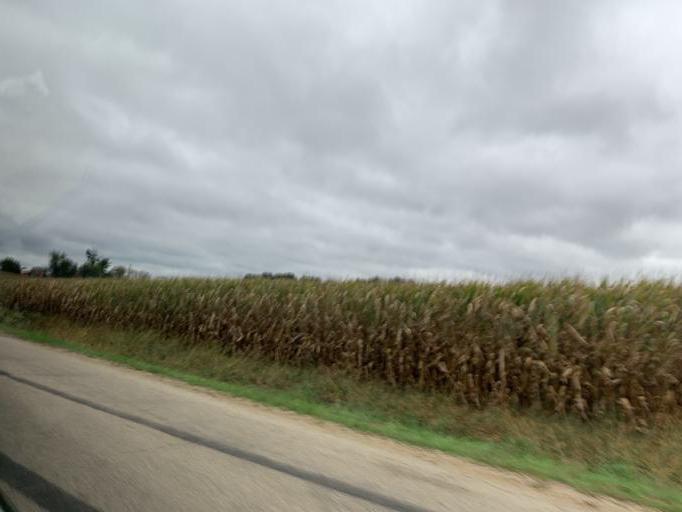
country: US
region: Wisconsin
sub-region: Sauk County
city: Prairie du Sac
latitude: 43.2831
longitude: -89.7789
